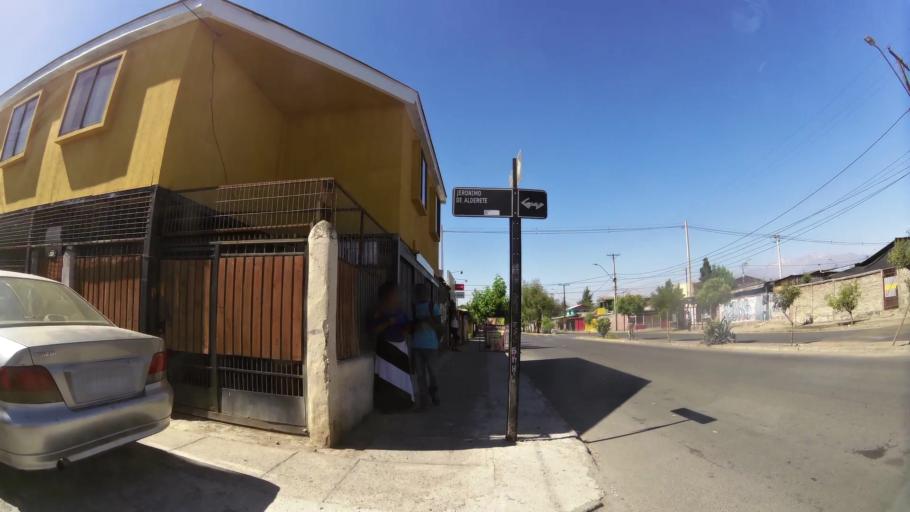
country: CL
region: Santiago Metropolitan
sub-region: Provincia de Maipo
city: San Bernardo
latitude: -33.5853
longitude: -70.6859
